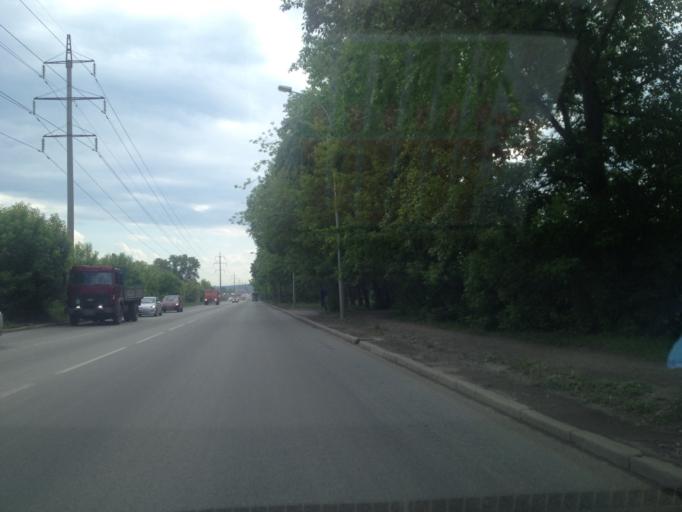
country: RU
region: Sverdlovsk
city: Sovkhoznyy
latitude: 56.7693
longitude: 60.5953
